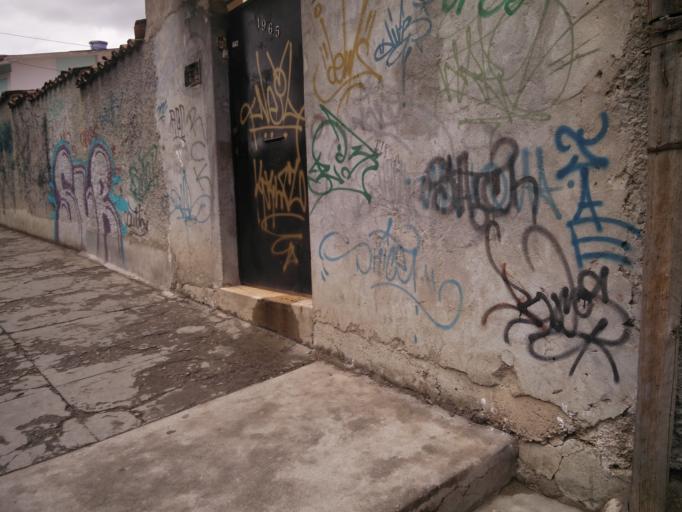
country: BO
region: La Paz
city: La Paz
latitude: -16.5087
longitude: -68.1325
